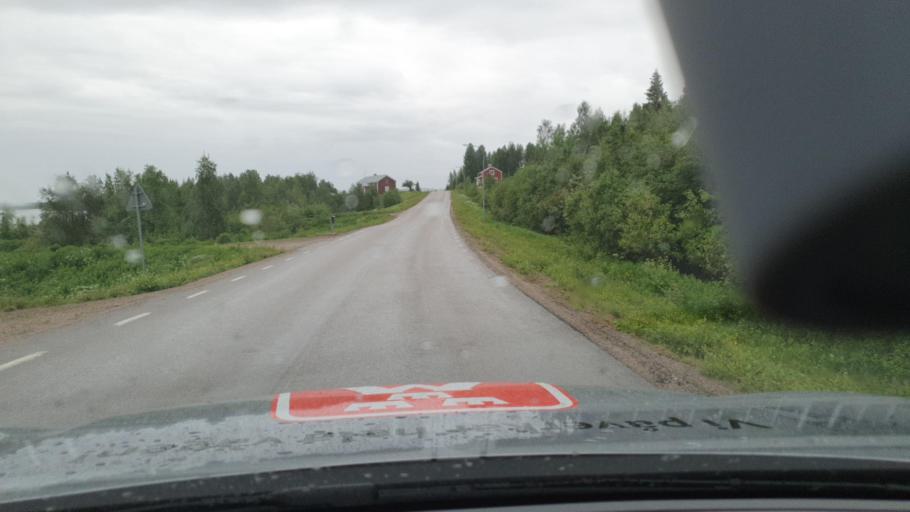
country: SE
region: Norrbotten
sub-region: Pajala Kommun
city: Pajala
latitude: 66.8080
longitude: 23.1203
